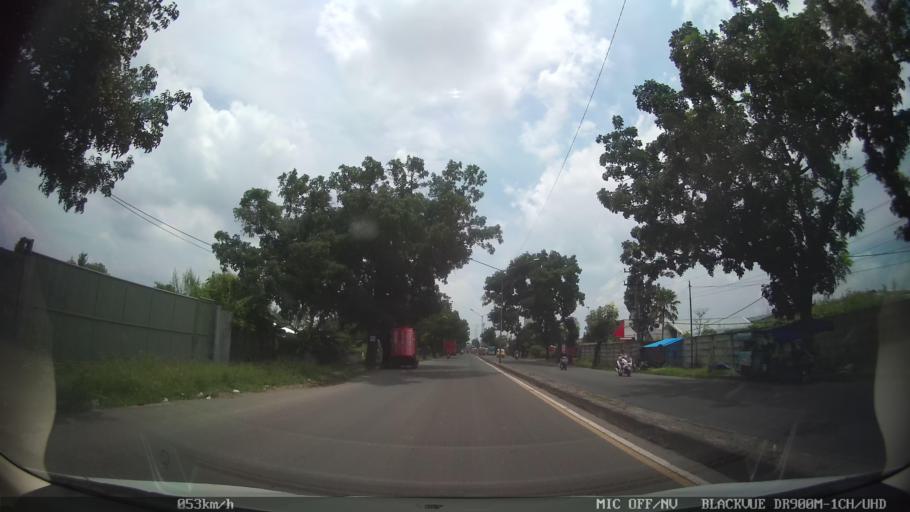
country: ID
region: North Sumatra
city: Labuhan Deli
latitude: 3.7007
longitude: 98.6763
